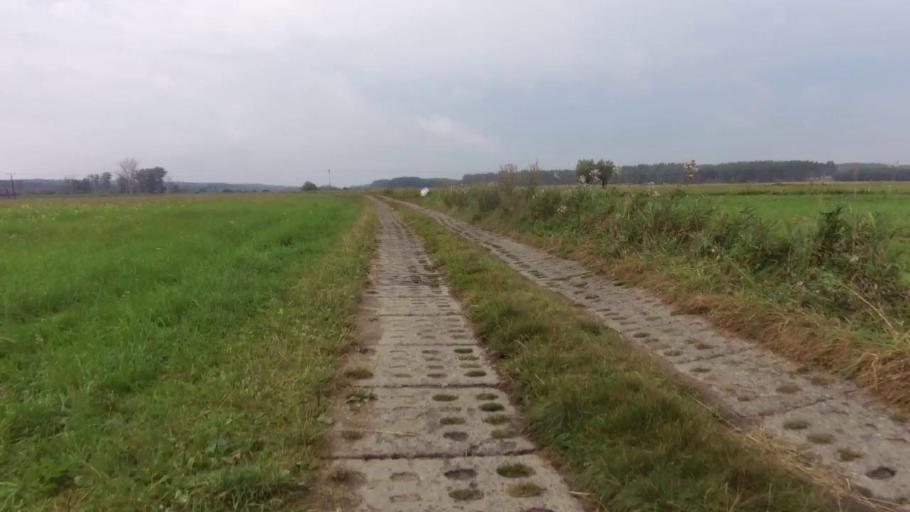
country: PL
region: West Pomeranian Voivodeship
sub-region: Powiat stargardzki
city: Suchan
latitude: 53.2517
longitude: 15.3926
